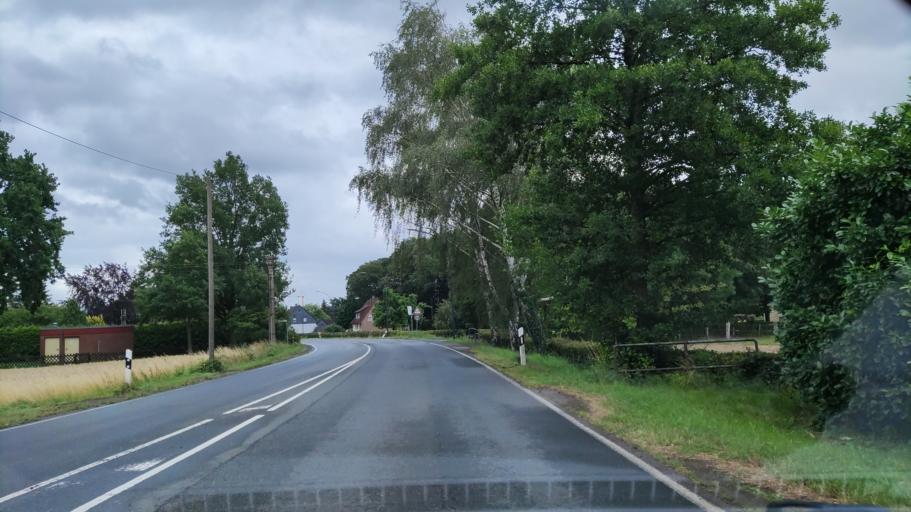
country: DE
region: North Rhine-Westphalia
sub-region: Regierungsbezirk Arnsberg
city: Hamm
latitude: 51.6695
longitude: 7.8748
